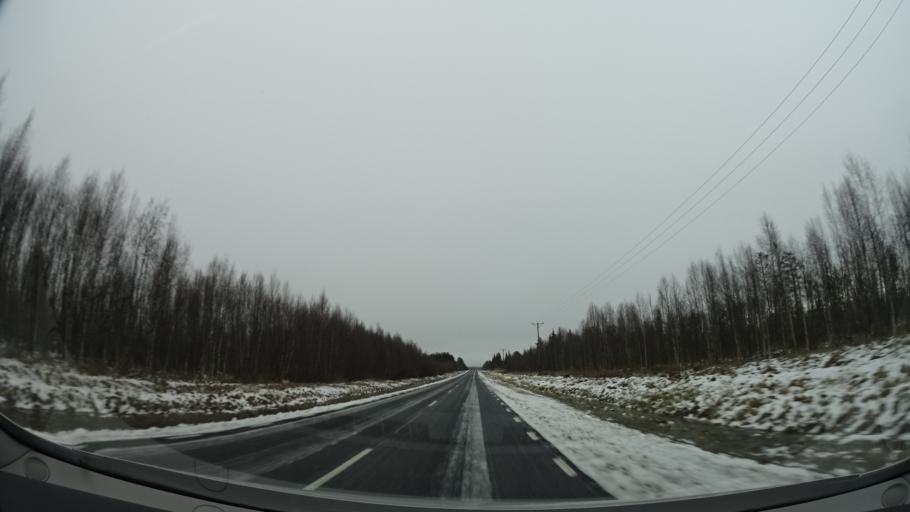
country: SE
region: Vaesterbotten
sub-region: Lycksele Kommun
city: Soderfors
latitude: 64.4621
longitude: 18.1579
